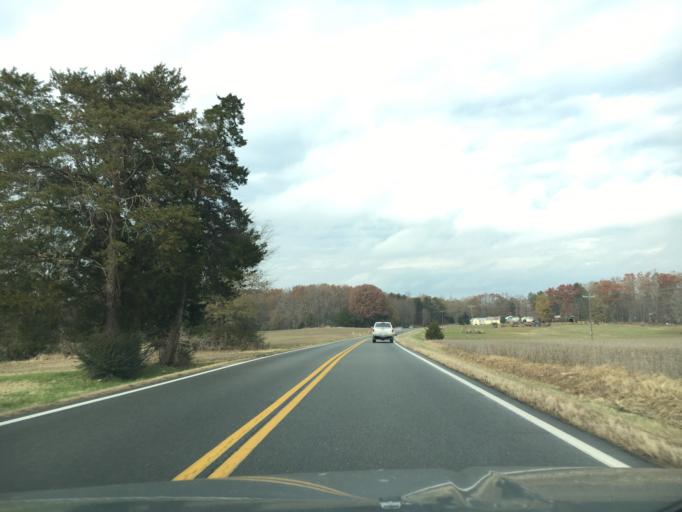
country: US
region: Virginia
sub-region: Prince Edward County
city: Farmville
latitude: 37.3794
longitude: -78.3719
